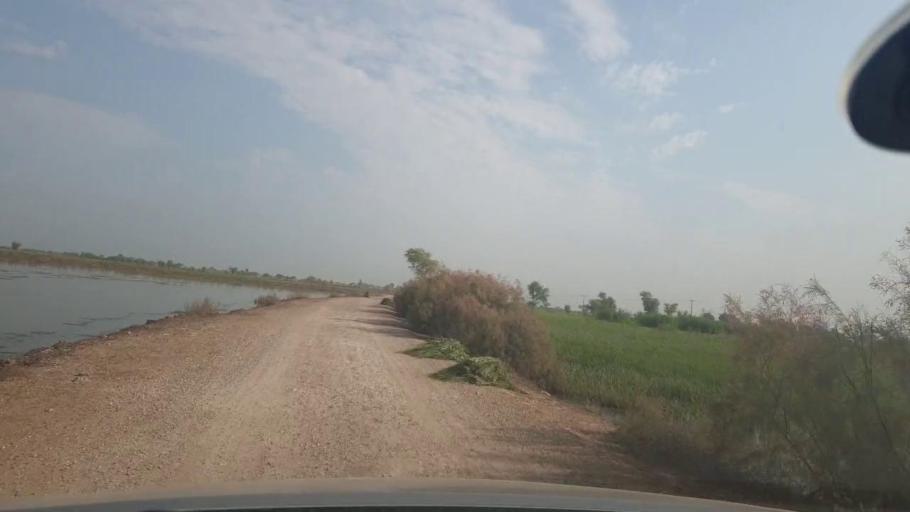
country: PK
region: Balochistan
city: Mehrabpur
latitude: 28.0655
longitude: 68.2100
